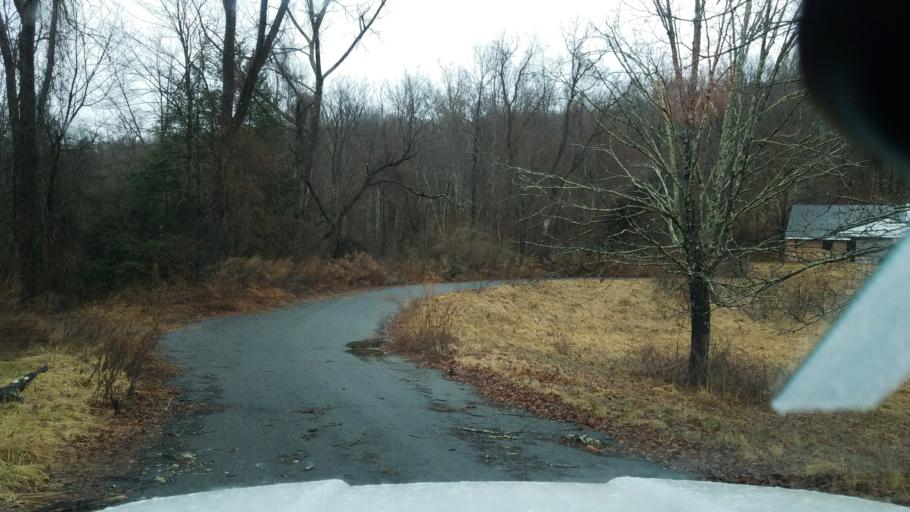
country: US
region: Connecticut
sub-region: New Haven County
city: Heritage Village
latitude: 41.4887
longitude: -73.2556
